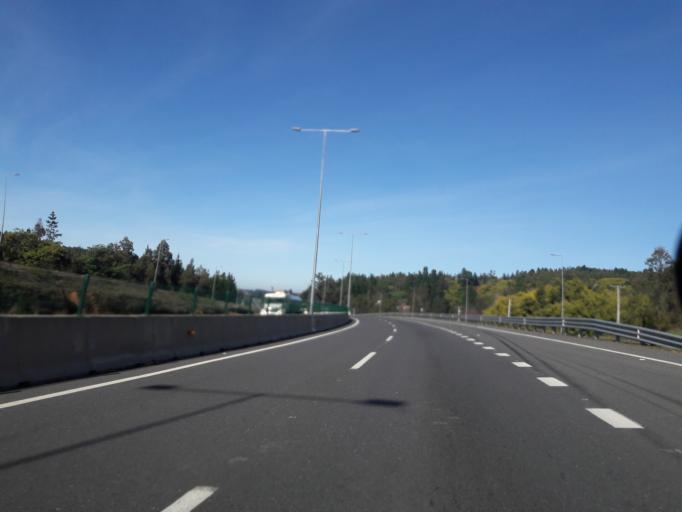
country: CL
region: Biobio
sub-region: Provincia de Biobio
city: Yumbel
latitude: -36.9354
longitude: -72.7614
